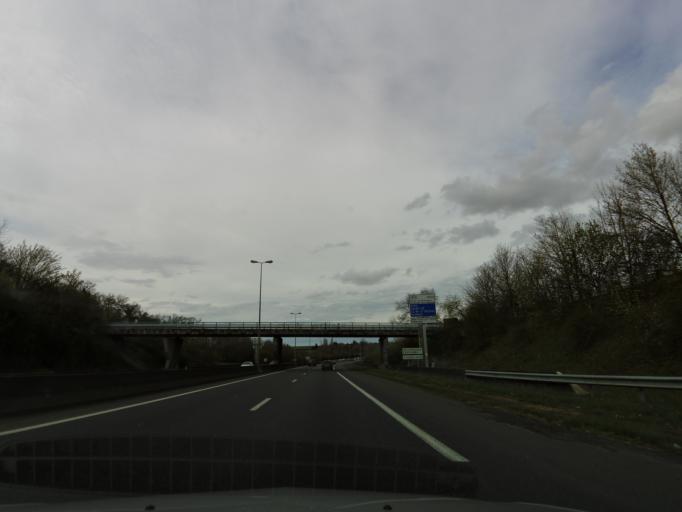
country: FR
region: Lower Normandy
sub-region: Departement du Calvados
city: Bretteville-sur-Odon
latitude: 49.1565
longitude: -0.4235
